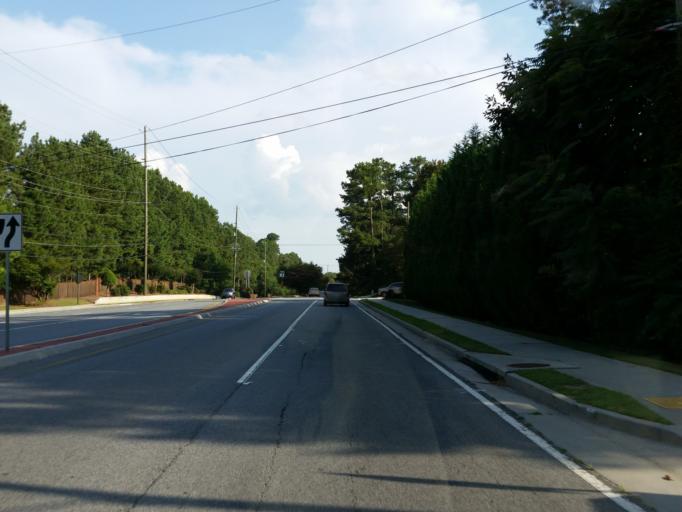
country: US
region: Georgia
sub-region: Cobb County
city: Vinings
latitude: 33.9371
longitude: -84.4612
